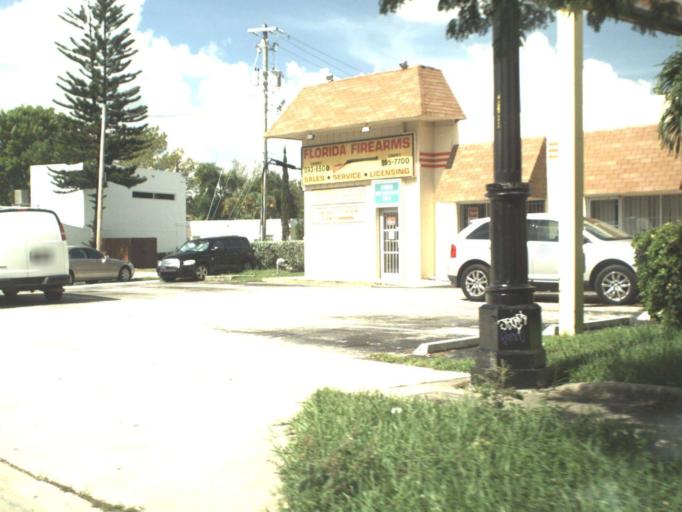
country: US
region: Florida
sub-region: Miami-Dade County
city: Biscayne Park
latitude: 25.8778
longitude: -80.1682
